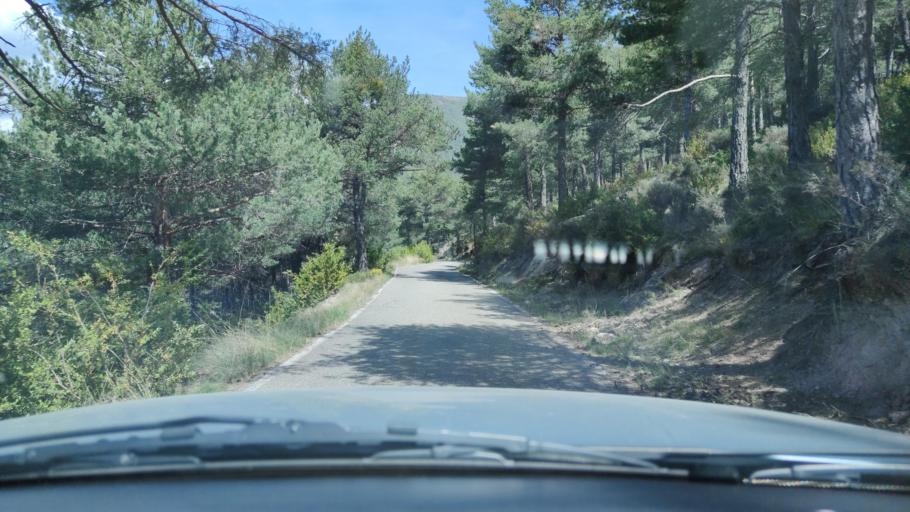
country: ES
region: Catalonia
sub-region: Provincia de Lleida
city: Sort
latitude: 42.3177
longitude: 1.1008
